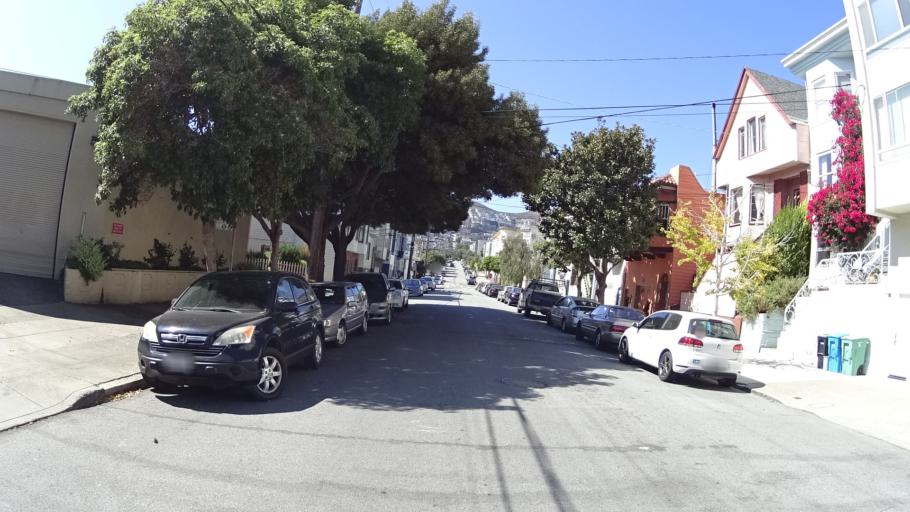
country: US
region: California
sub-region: San Francisco County
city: San Francisco
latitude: 37.7523
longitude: -122.4307
